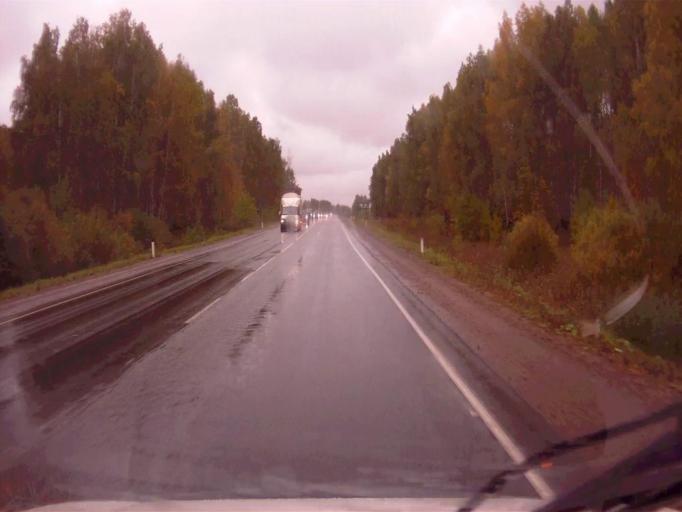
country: RU
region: Chelyabinsk
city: Argayash
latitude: 55.4664
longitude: 60.9100
